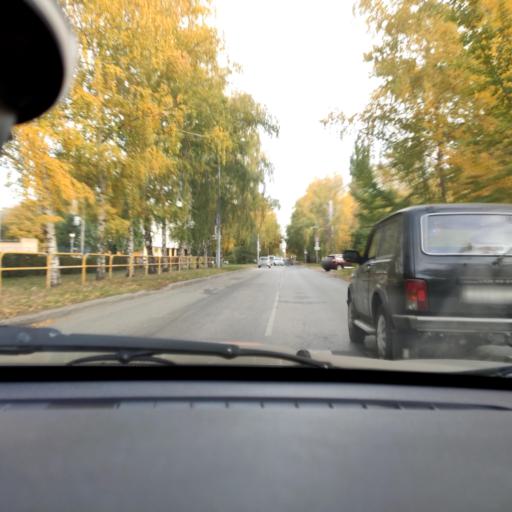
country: RU
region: Samara
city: Tol'yatti
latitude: 53.5094
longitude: 49.2837
